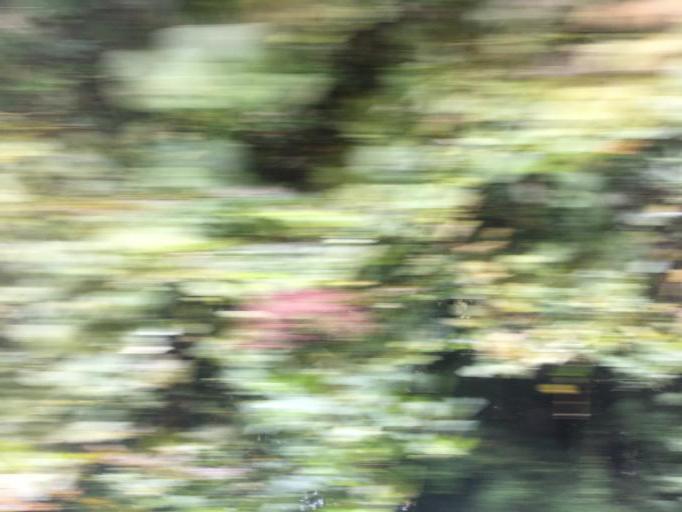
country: JP
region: Niigata
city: Murakami
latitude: 38.0786
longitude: 139.6485
